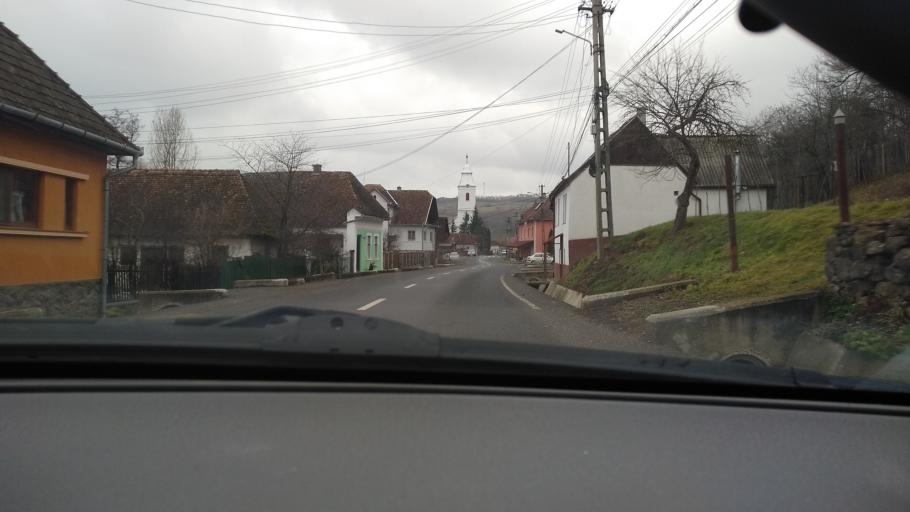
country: RO
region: Mures
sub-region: Comuna Magherani
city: Magherani
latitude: 46.5642
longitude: 24.9072
